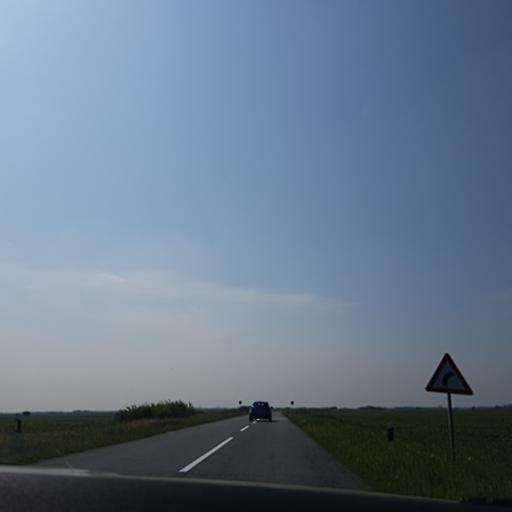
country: RS
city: Jarkovac
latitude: 45.3031
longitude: 20.7603
